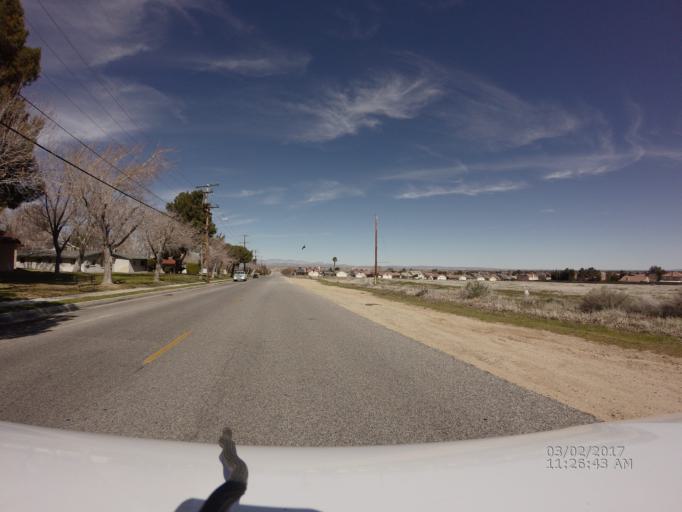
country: US
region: California
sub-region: Los Angeles County
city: Quartz Hill
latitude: 34.6472
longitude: -118.2449
